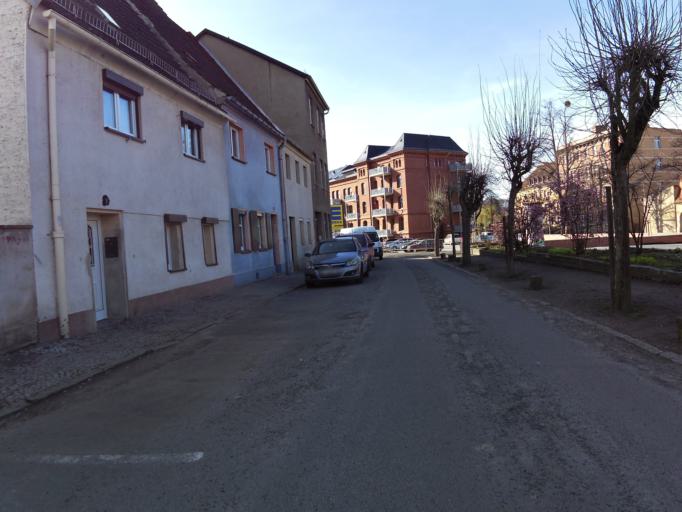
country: DE
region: Saxony
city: Torgau
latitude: 51.5608
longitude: 13.0029
